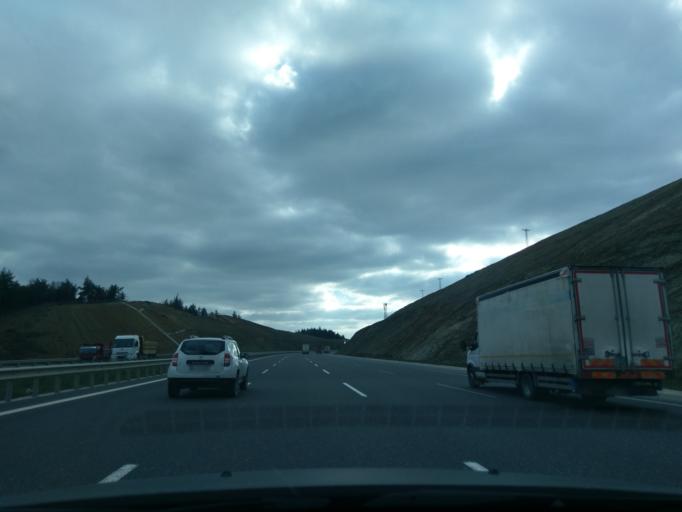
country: TR
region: Istanbul
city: Basaksehir
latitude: 41.1631
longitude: 28.8096
